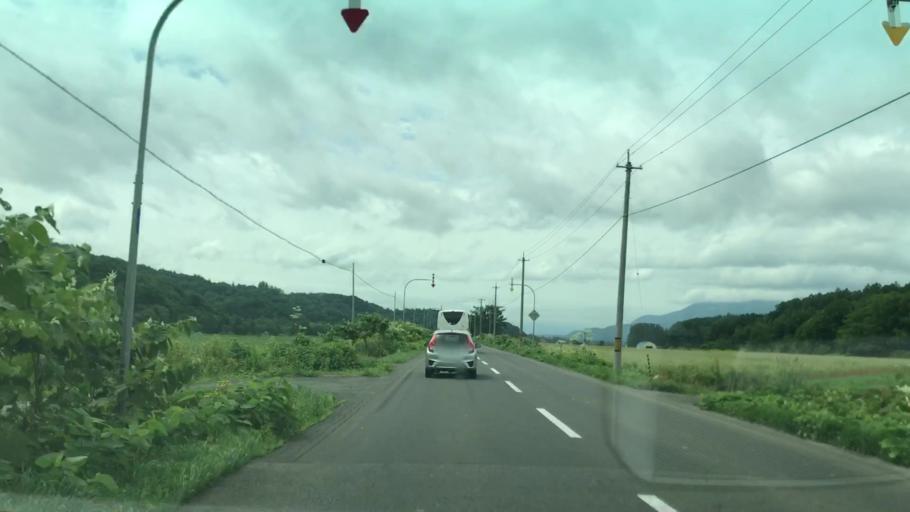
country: JP
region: Hokkaido
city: Niseko Town
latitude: 42.9454
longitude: 140.8220
